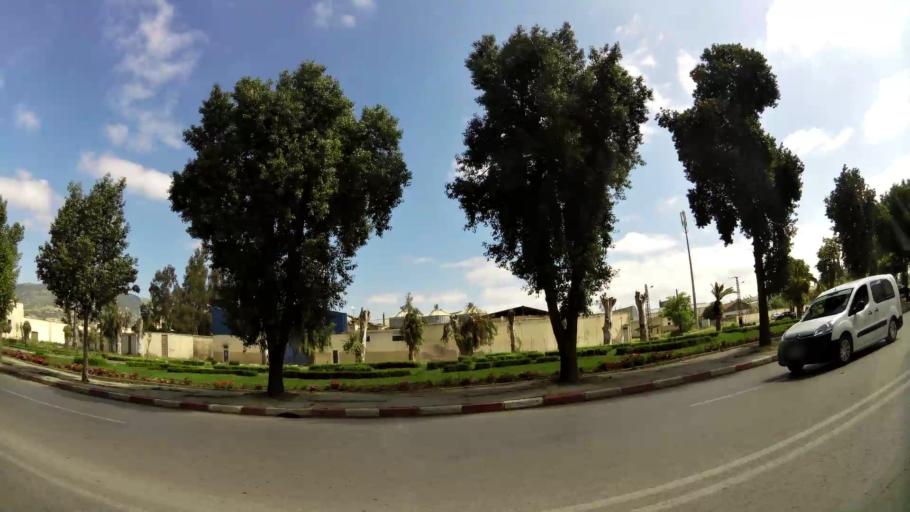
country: MA
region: Fes-Boulemane
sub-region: Fes
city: Fes
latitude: 34.0399
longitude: -5.0333
